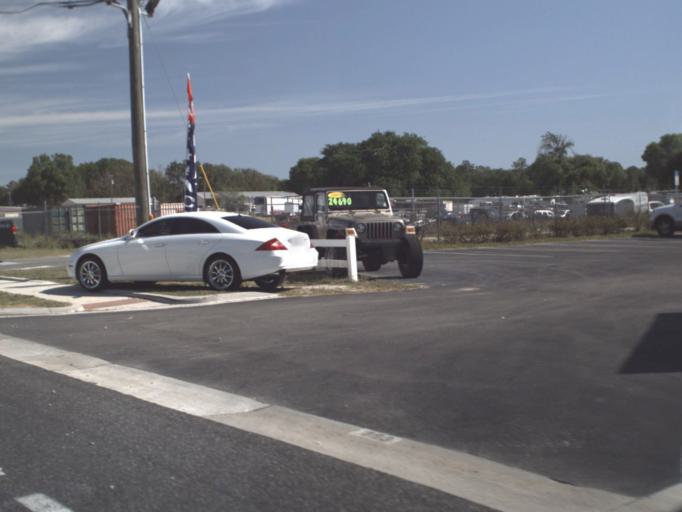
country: US
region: Florida
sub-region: Lake County
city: Fruitland Park
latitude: 28.8758
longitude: -81.9064
